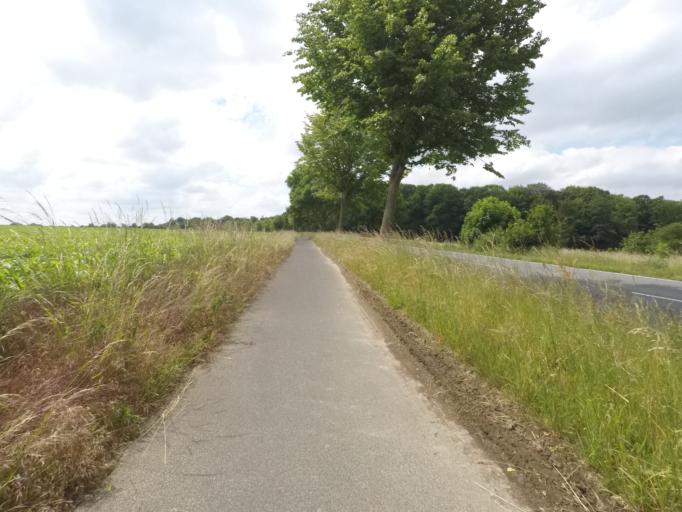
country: DE
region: North Rhine-Westphalia
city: Spenge
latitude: 52.1103
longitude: 8.4707
